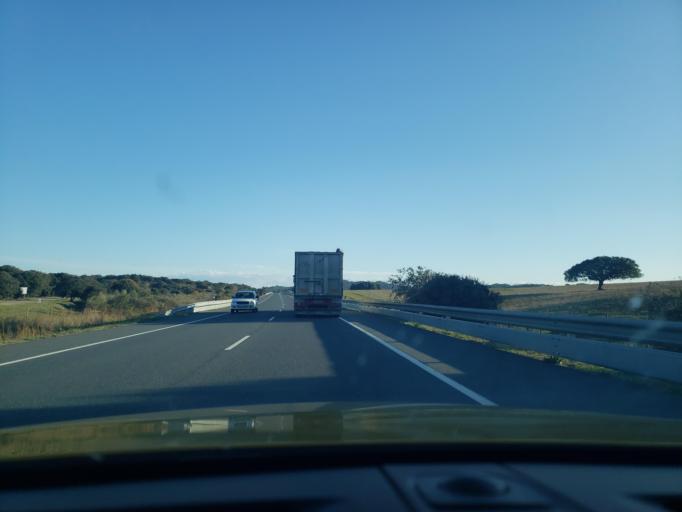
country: PT
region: Evora
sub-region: Portel
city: Portel
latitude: 38.3750
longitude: -7.7071
